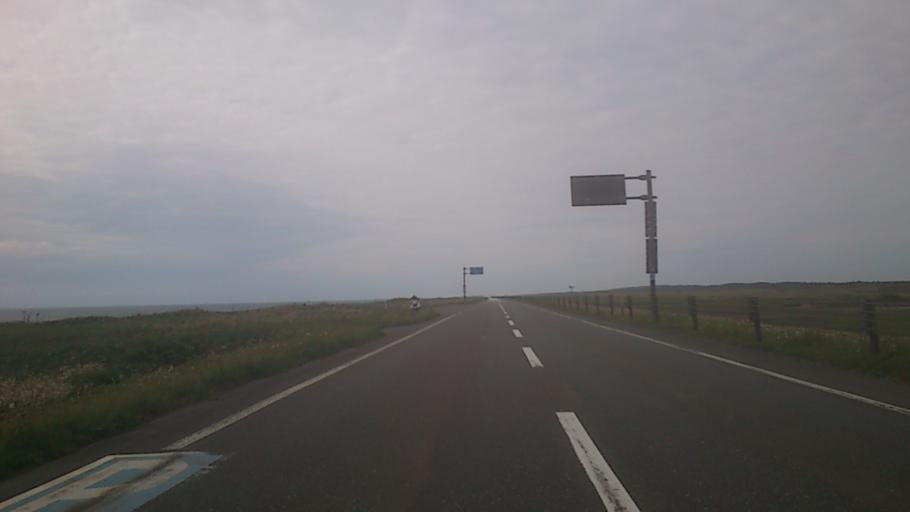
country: JP
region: Hokkaido
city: Wakkanai
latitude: 45.0432
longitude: 141.6575
